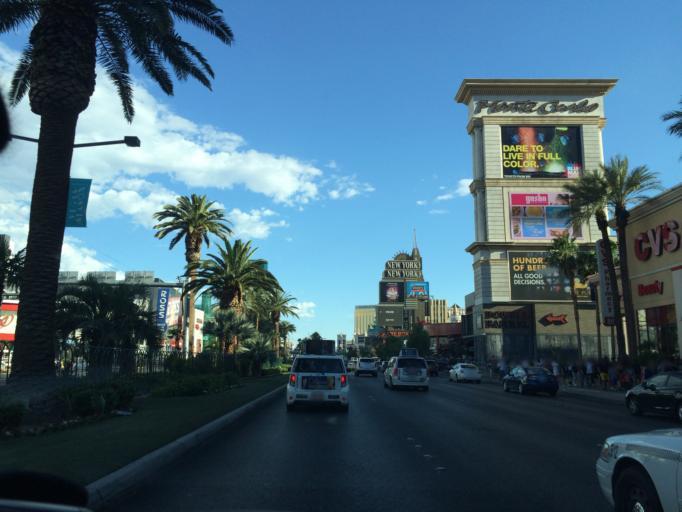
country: US
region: Nevada
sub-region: Clark County
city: Paradise
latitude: 36.1060
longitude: -115.1731
